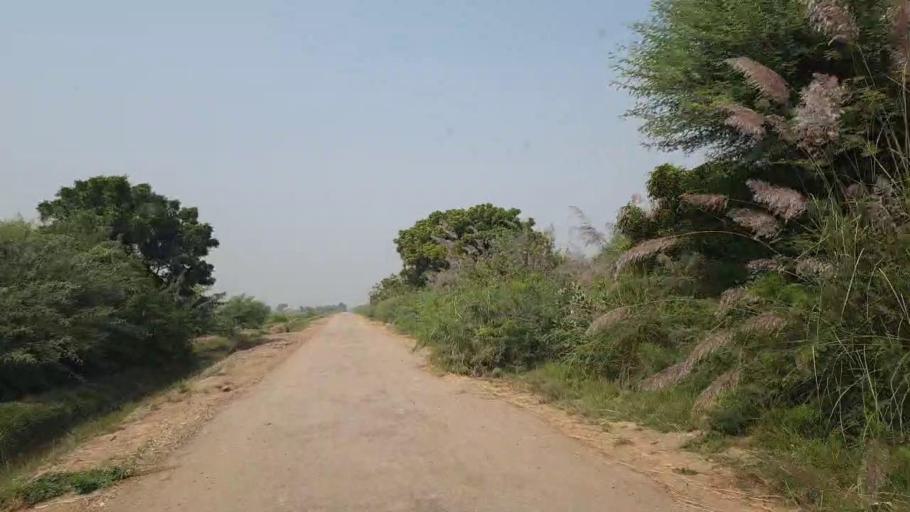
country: PK
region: Sindh
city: Matli
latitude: 25.1438
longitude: 68.7055
